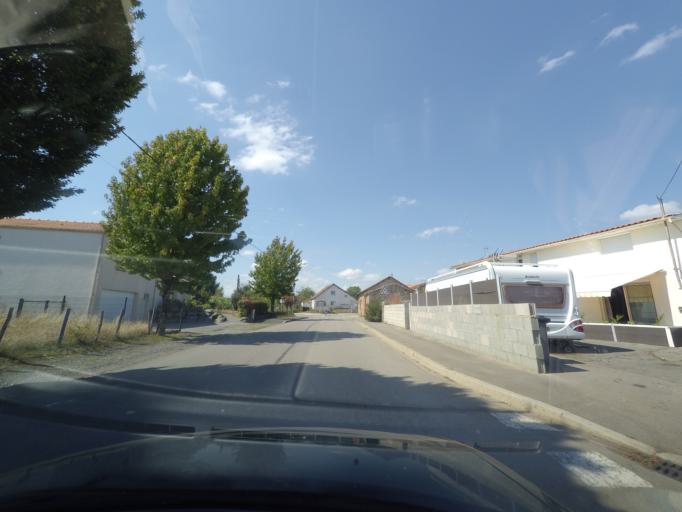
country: FR
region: Pays de la Loire
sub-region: Departement de la Loire-Atlantique
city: Saint-Lumine-de-Coutais
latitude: 47.0530
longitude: -1.7259
